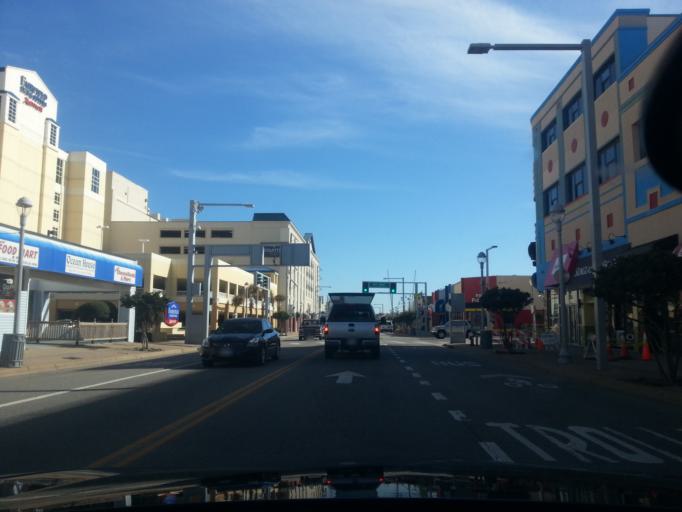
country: US
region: Virginia
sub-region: City of Virginia Beach
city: Virginia Beach
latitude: 36.8478
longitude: -75.9749
